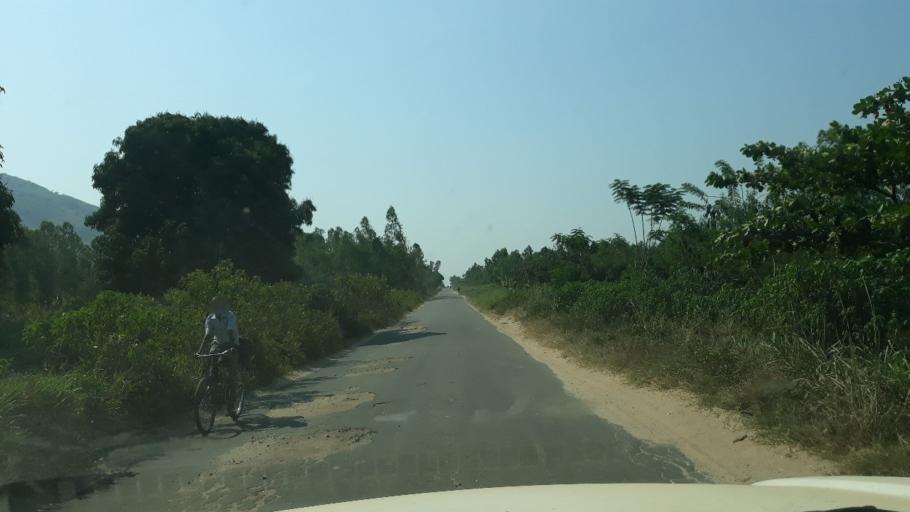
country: CD
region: South Kivu
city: Uvira
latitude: -3.3068
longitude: 29.1600
